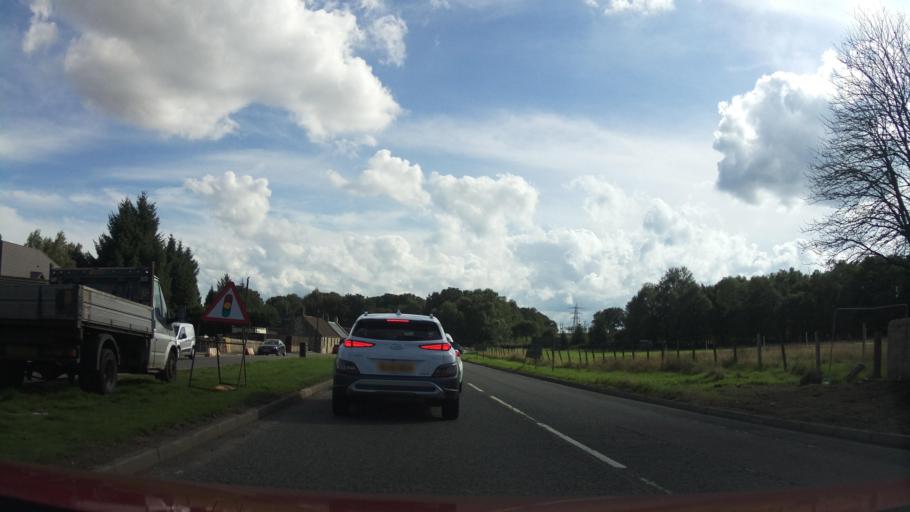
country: GB
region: Scotland
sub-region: Stirling
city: Cowie
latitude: 56.0411
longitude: -3.8603
